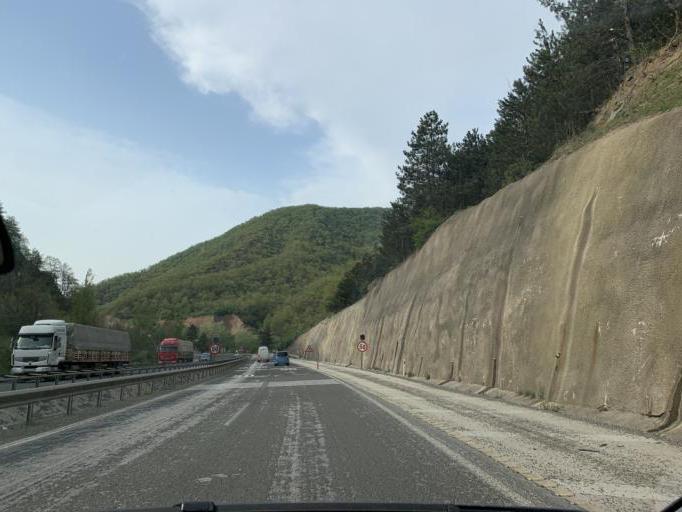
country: TR
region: Bursa
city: Kursunlu
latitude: 39.9952
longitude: 29.6530
